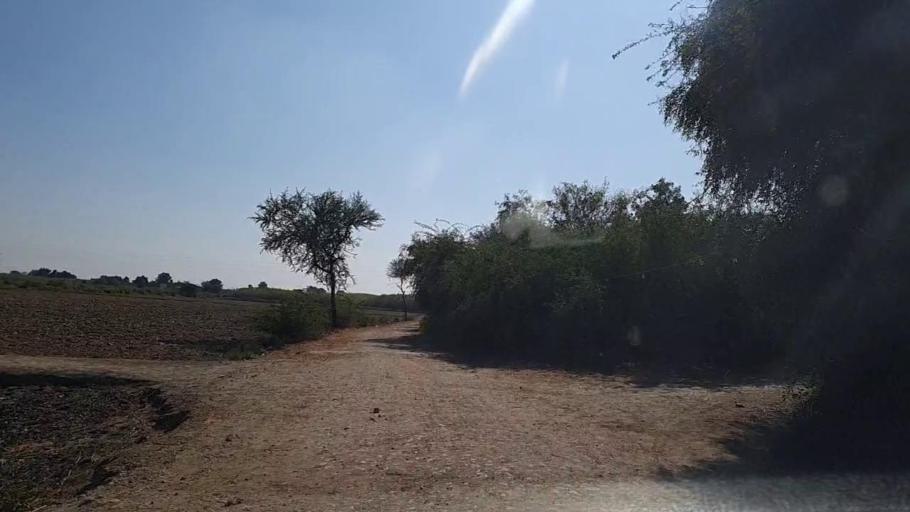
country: PK
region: Sindh
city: Mirpur Batoro
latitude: 24.6893
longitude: 68.1855
